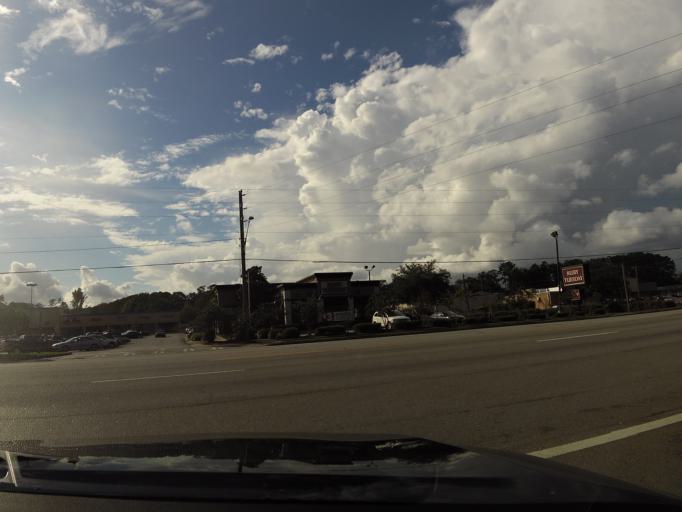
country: US
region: Georgia
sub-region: Liberty County
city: Hinesville
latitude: 31.8360
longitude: -81.5957
